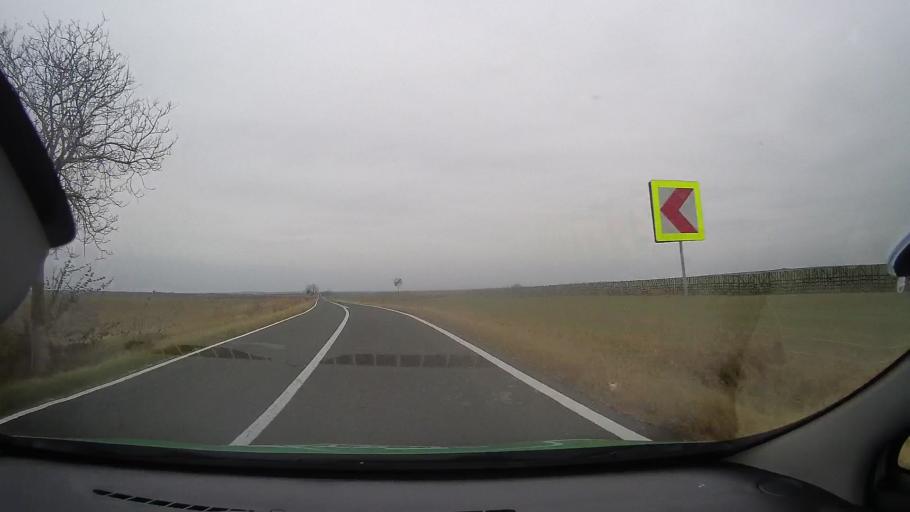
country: RO
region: Constanta
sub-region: Comuna Saraiu
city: Saraiu
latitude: 44.7109
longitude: 28.1063
